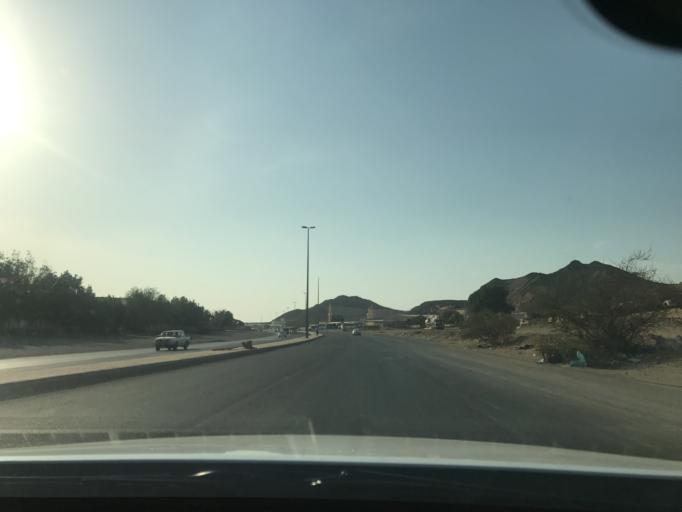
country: SA
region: Makkah
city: Jeddah
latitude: 21.4078
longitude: 39.4267
